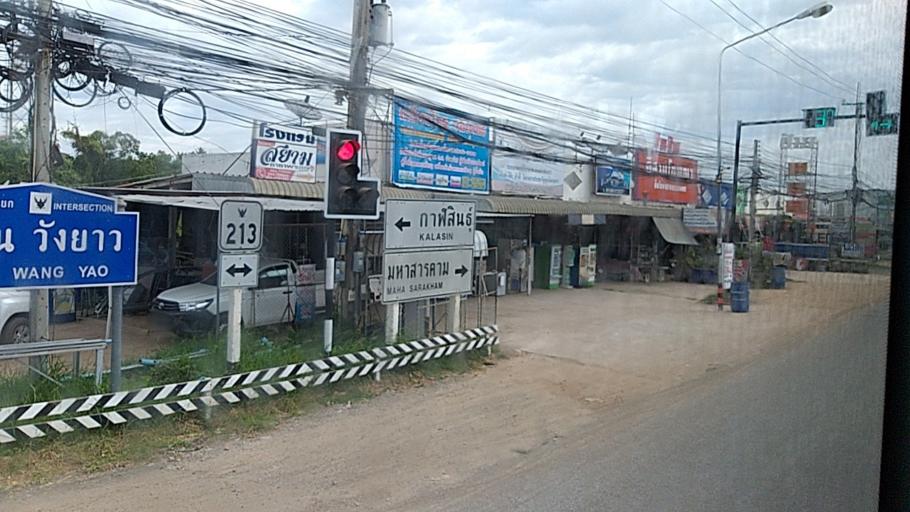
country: TH
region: Maha Sarakham
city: Maha Sarakham
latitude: 16.2150
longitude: 103.2789
